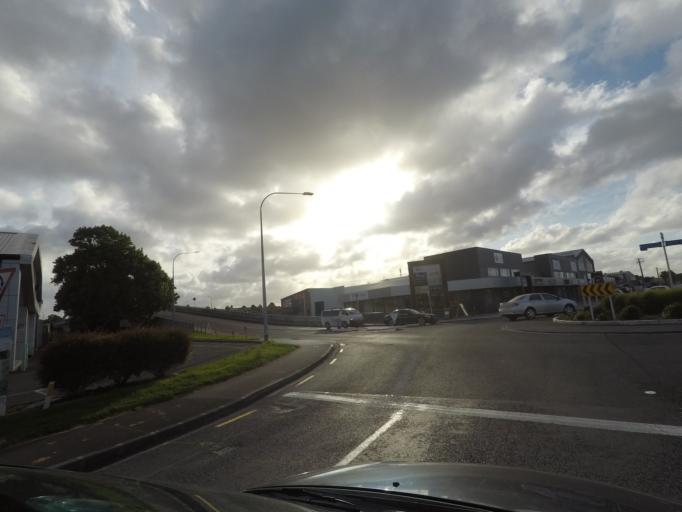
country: NZ
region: Auckland
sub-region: Auckland
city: Auckland
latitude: -36.9145
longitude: 174.7545
